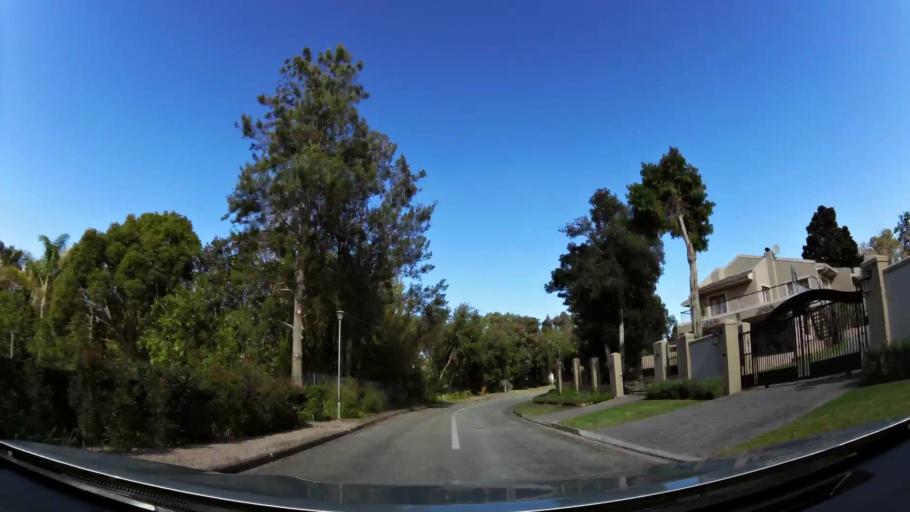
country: ZA
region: Western Cape
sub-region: Eden District Municipality
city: George
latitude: -33.9440
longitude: 22.4667
